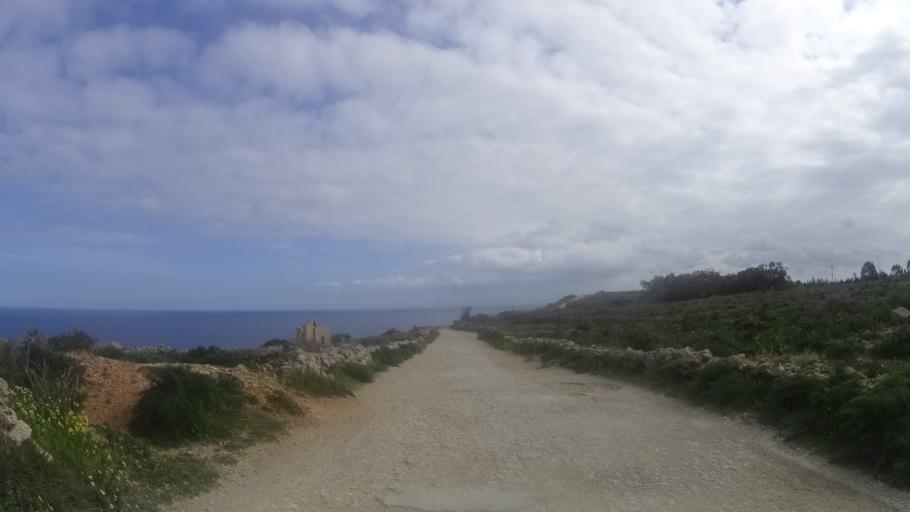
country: MT
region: Il-Qala
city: Qala
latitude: 36.0409
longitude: 14.3202
